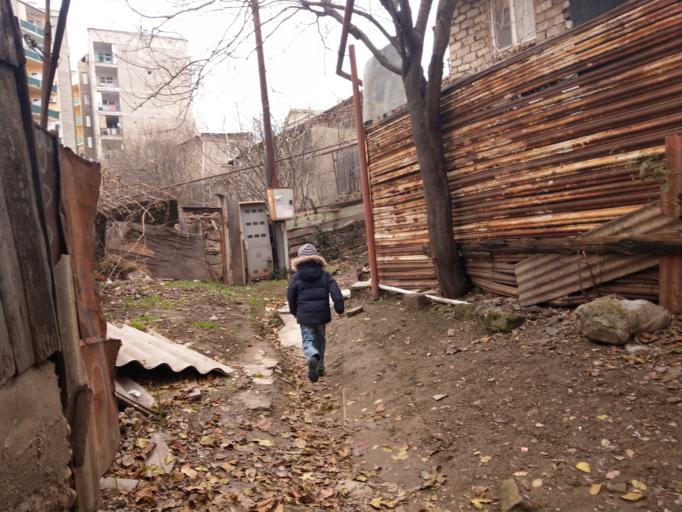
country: GE
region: T'bilisi
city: Tbilisi
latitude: 41.7225
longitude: 44.7669
